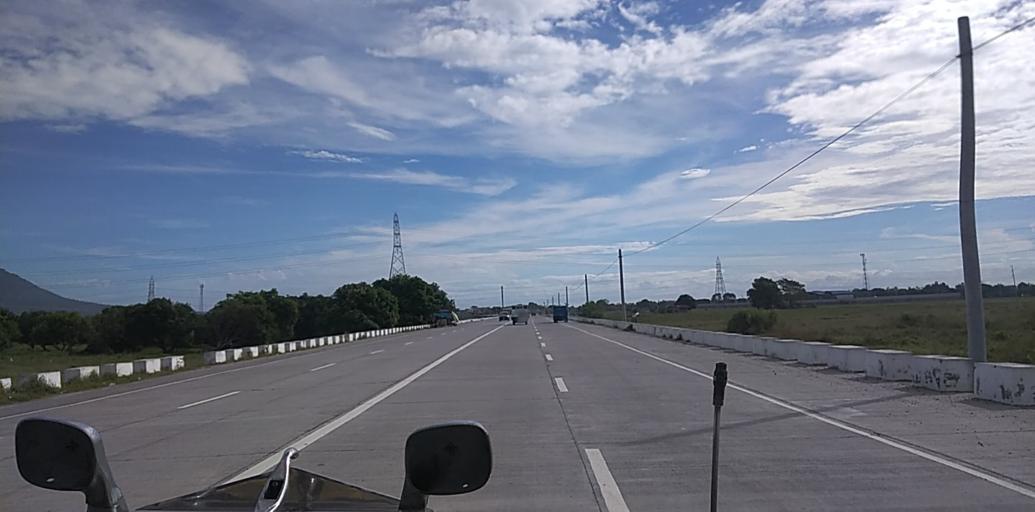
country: PH
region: Central Luzon
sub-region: Province of Pampanga
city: Anao
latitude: 15.1354
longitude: 120.6864
